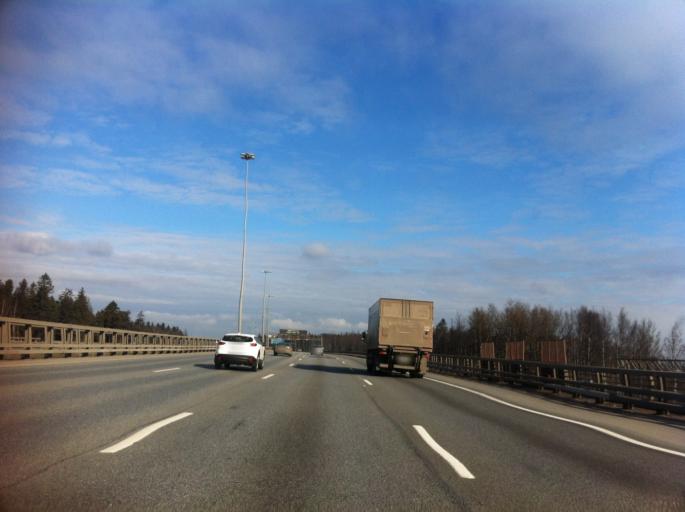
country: RU
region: St.-Petersburg
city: Krasnogvargeisky
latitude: 59.9306
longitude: 30.5364
